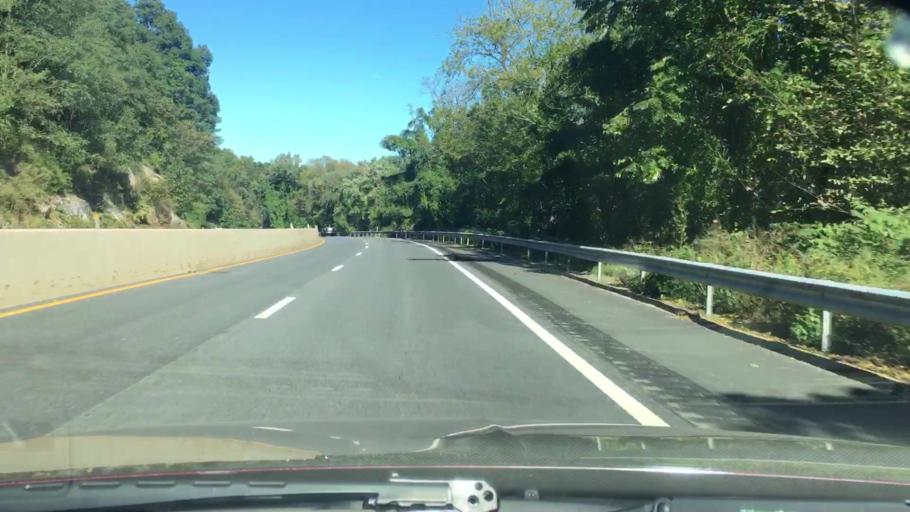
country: US
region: New York
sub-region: Westchester County
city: Chappaqua
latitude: 41.1503
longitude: -73.7826
